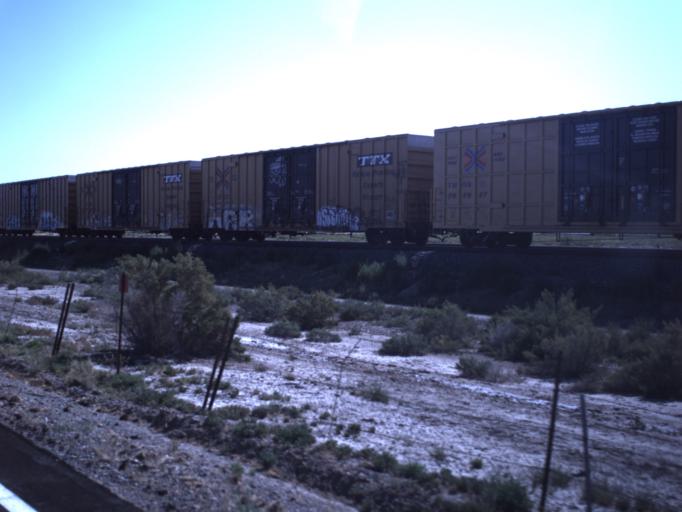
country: US
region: Utah
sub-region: Millard County
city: Delta
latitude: 39.2343
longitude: -112.6667
